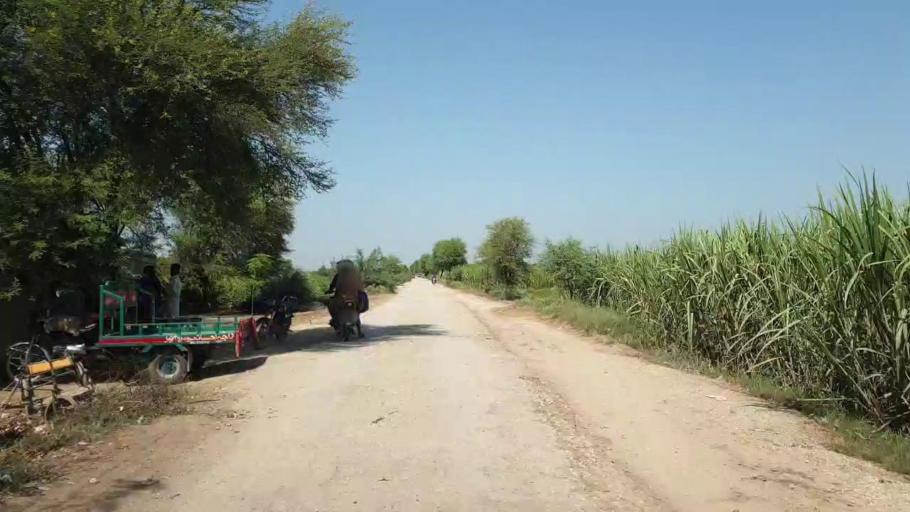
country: PK
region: Sindh
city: Tando Jam
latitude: 25.4871
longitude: 68.4632
